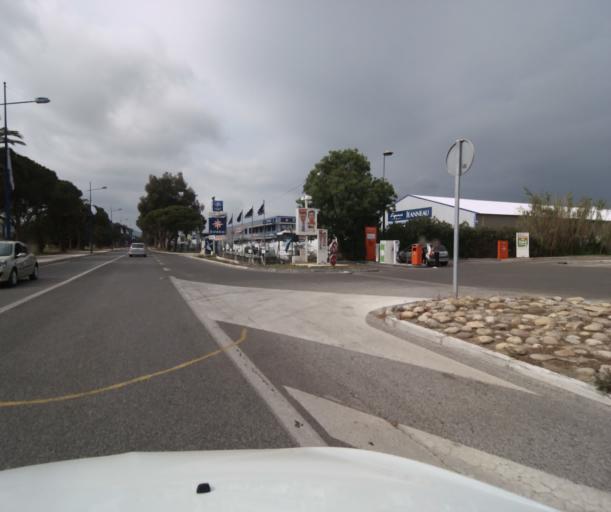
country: FR
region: Provence-Alpes-Cote d'Azur
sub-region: Departement du Var
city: Hyeres
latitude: 43.0848
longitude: 6.1483
